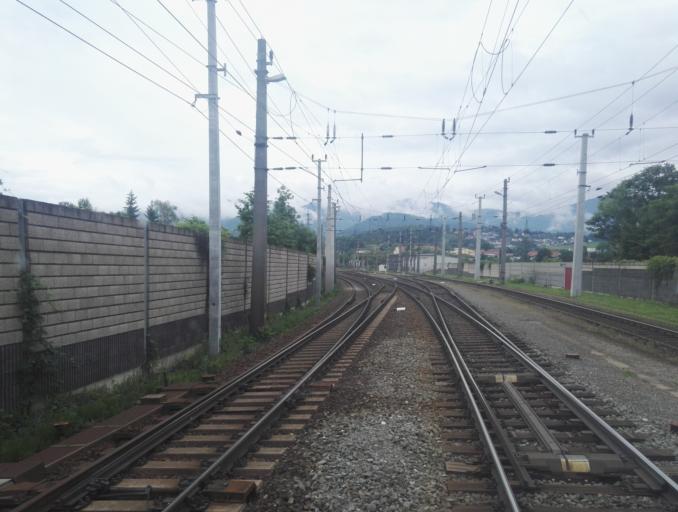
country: AT
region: Styria
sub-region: Politischer Bezirk Bruck-Muerzzuschlag
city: Bruck an der Mur
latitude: 47.4310
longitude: 15.2748
